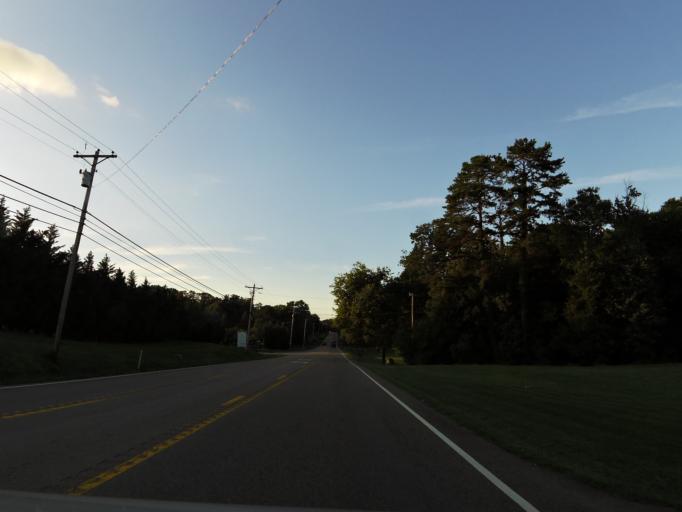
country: US
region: Tennessee
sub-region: Loudon County
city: Lenoir City
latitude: 35.8483
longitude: -84.2261
